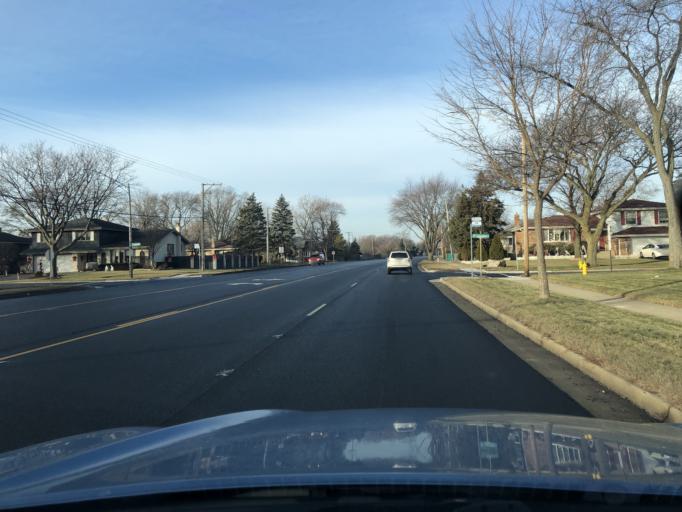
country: US
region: Illinois
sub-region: Cook County
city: Mount Prospect
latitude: 42.0473
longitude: -87.9508
